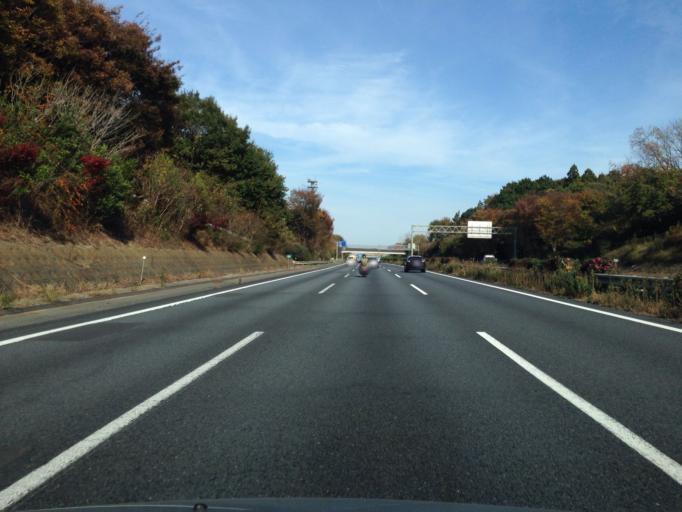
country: JP
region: Ibaraki
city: Ishioka
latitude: 36.1755
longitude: 140.2461
